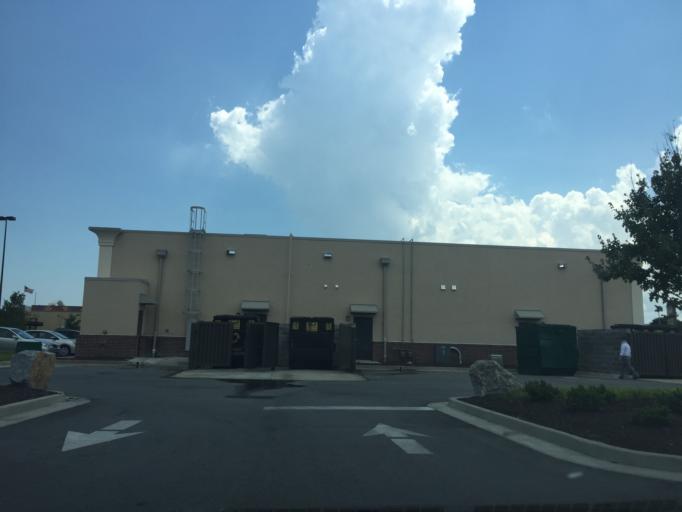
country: US
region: Georgia
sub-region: Chatham County
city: Isle of Hope
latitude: 32.0057
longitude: -81.1138
